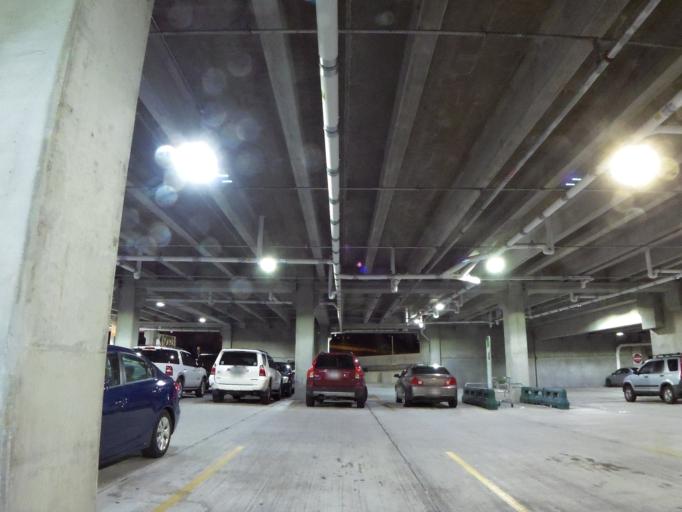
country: US
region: Tennessee
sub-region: Knox County
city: Knoxville
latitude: 35.9494
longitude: -83.9400
